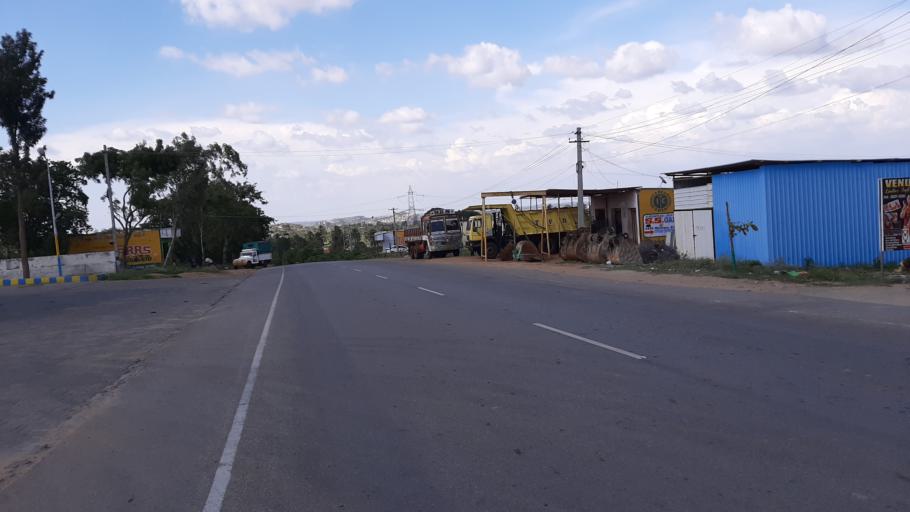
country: IN
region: Tamil Nadu
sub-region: Krishnagiri
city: Denkanikota
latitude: 12.5388
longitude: 77.7888
